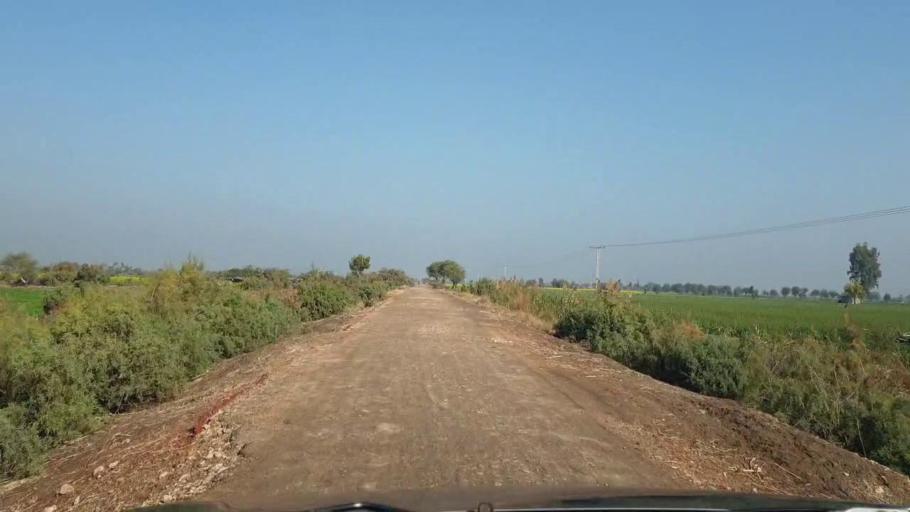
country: PK
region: Sindh
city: Sinjhoro
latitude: 26.0508
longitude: 68.7885
